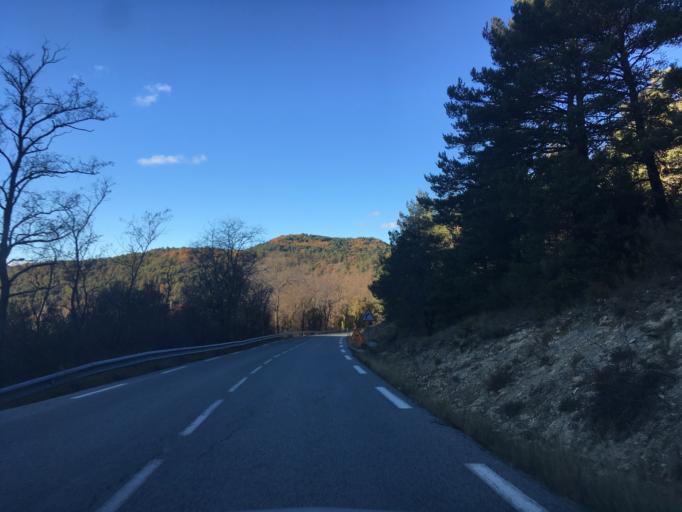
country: FR
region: Provence-Alpes-Cote d'Azur
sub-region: Departement des Alpes-de-Haute-Provence
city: Castellane
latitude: 43.7383
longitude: 6.4997
